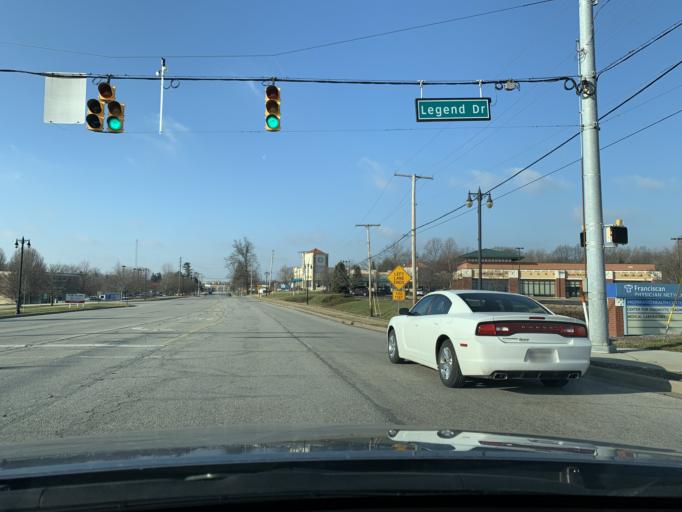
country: US
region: Indiana
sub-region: Porter County
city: Valparaiso
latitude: 41.4685
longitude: -87.0304
